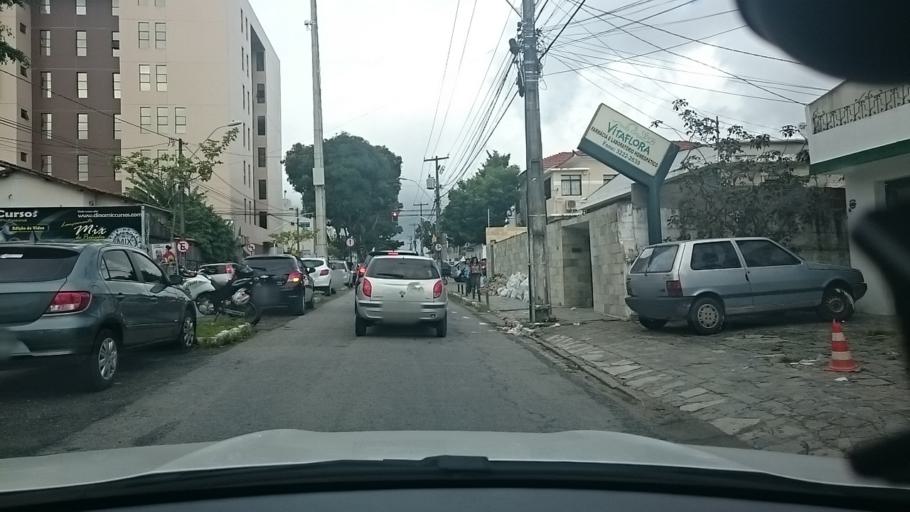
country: BR
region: Paraiba
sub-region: Joao Pessoa
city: Joao Pessoa
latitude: -7.1177
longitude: -34.8770
